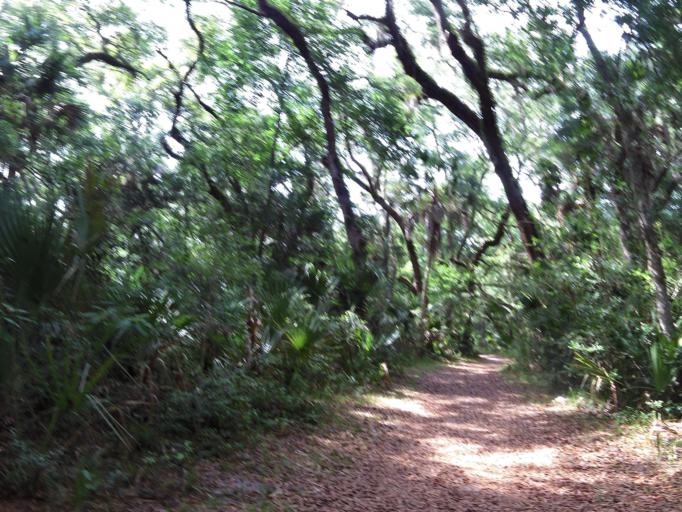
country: US
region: Florida
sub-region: Flagler County
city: Palm Coast
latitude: 29.6361
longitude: -81.2104
